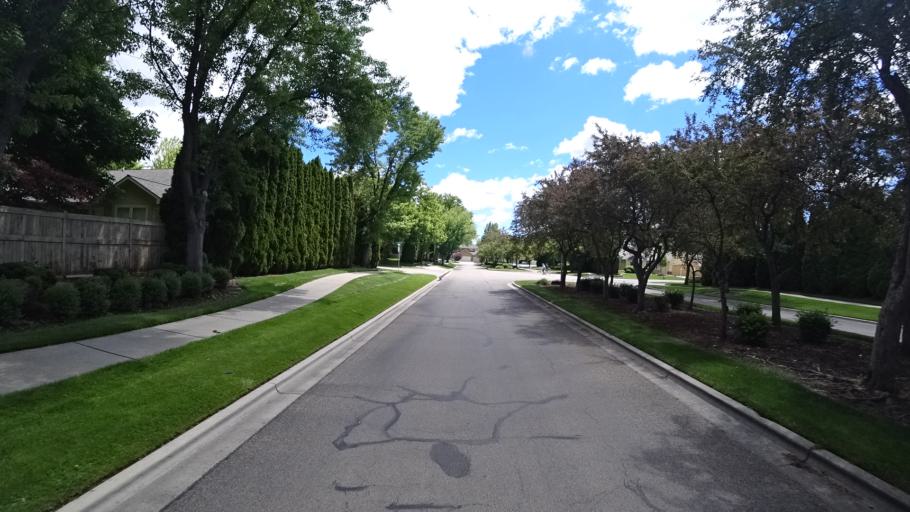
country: US
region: Idaho
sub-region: Ada County
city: Eagle
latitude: 43.6583
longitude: -116.3509
